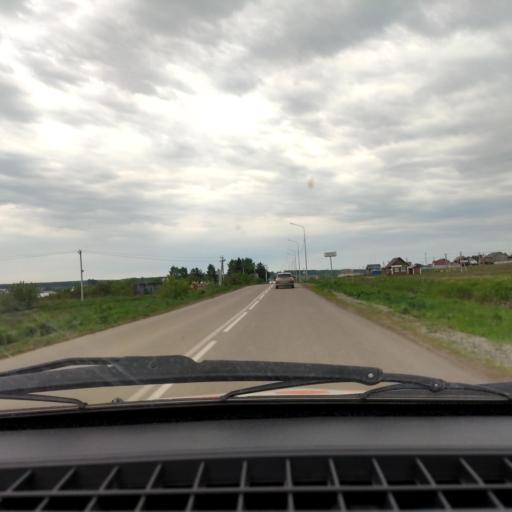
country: RU
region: Bashkortostan
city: Avdon
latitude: 54.5577
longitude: 55.7629
